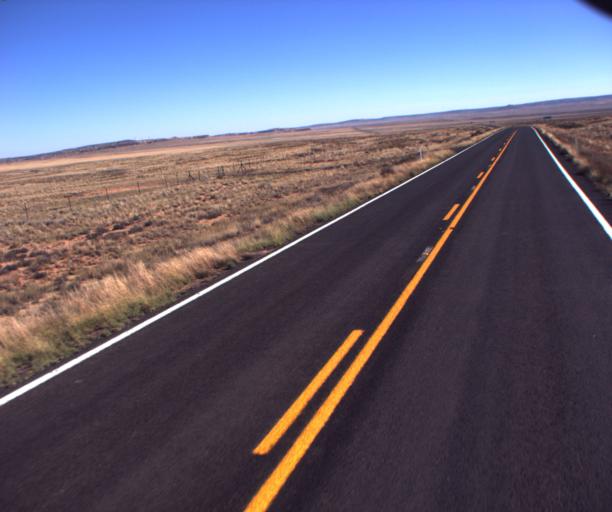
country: US
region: Arizona
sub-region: Navajo County
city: First Mesa
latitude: 35.9694
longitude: -110.8118
